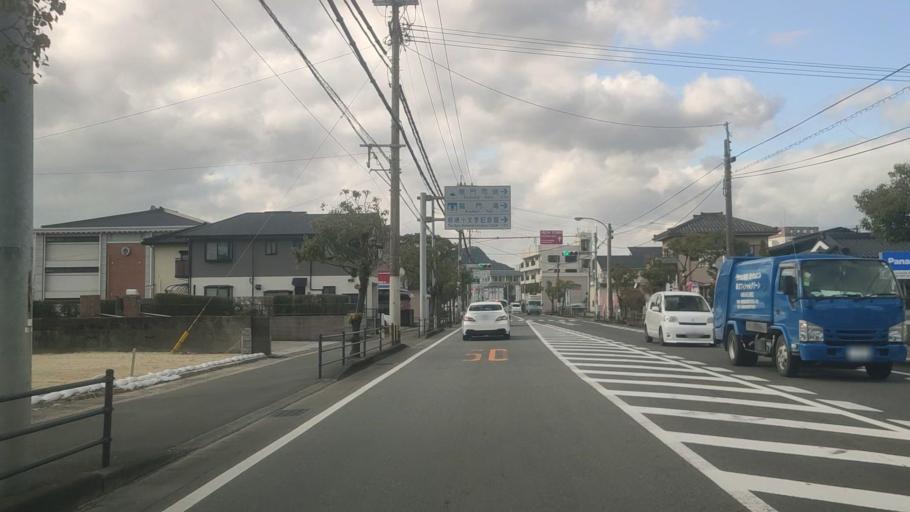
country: JP
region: Kagoshima
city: Kajiki
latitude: 31.7337
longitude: 130.6700
